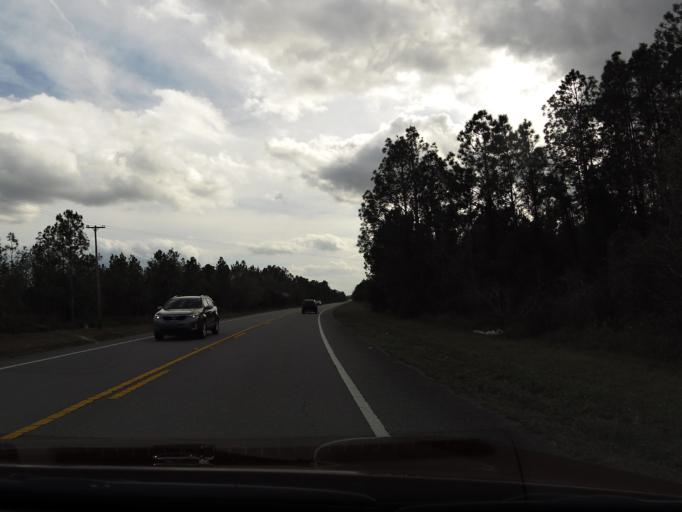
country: US
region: Florida
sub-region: Volusia County
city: De Leon Springs
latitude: 29.2525
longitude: -81.3264
